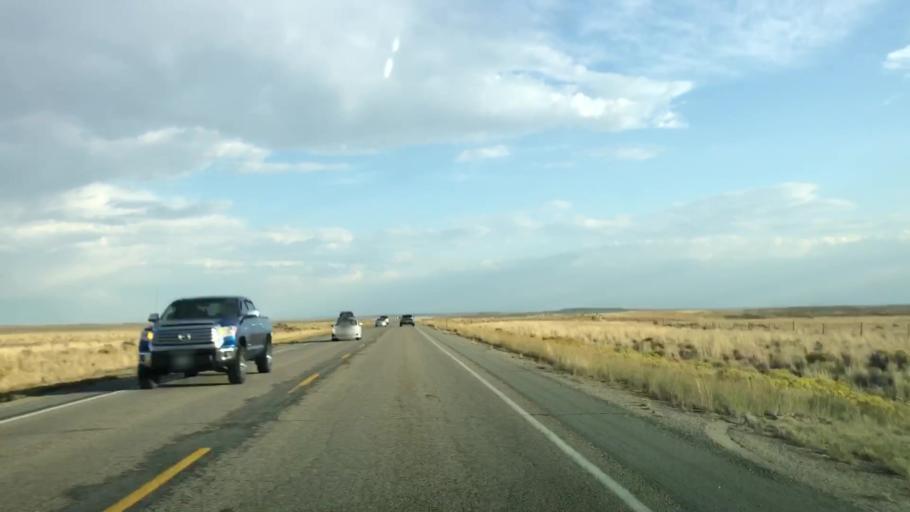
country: US
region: Wyoming
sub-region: Sublette County
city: Pinedale
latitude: 42.4011
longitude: -109.5467
